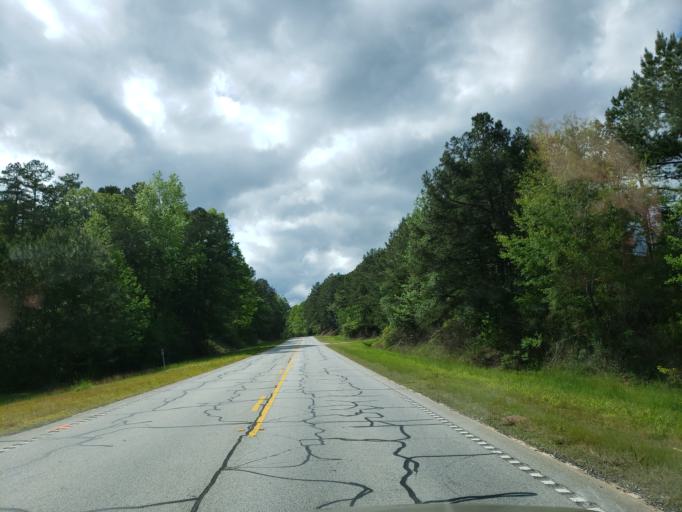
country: US
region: Georgia
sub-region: Haralson County
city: Tallapoosa
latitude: 33.7433
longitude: -85.3397
